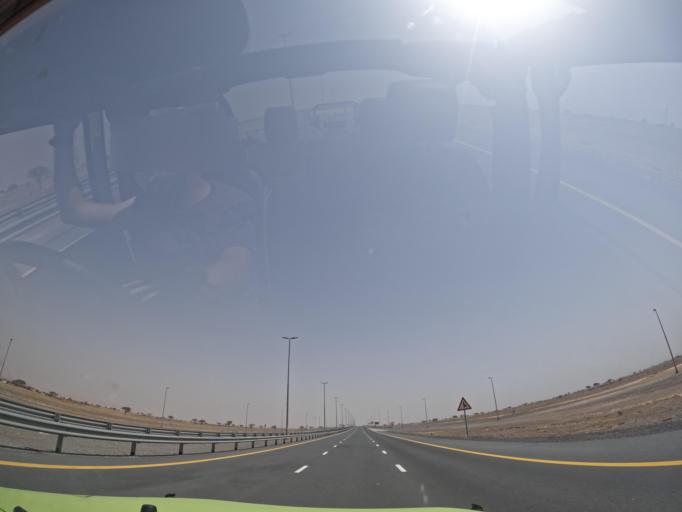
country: AE
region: Ash Shariqah
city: Adh Dhayd
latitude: 24.9764
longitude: 55.8526
